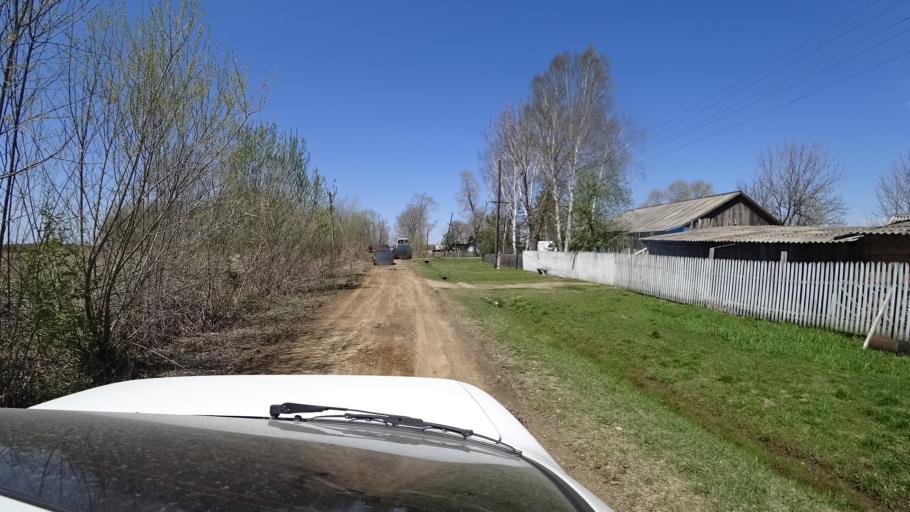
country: RU
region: Primorskiy
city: Lazo
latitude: 45.8000
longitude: 133.7606
